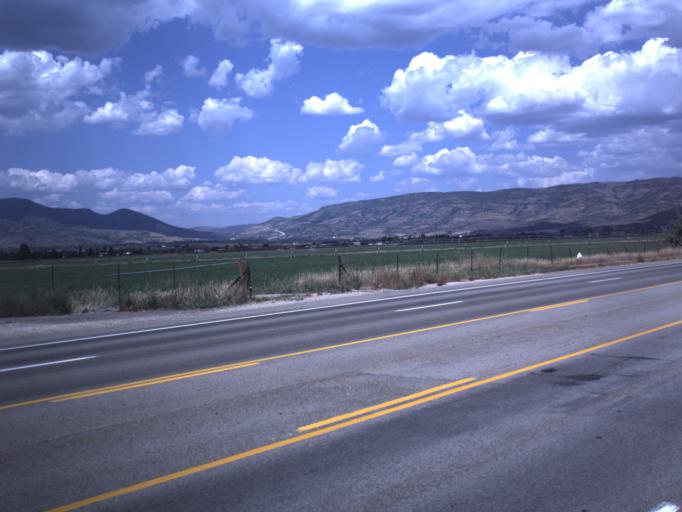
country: US
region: Utah
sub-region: Wasatch County
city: Heber
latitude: 40.4762
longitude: -111.4392
